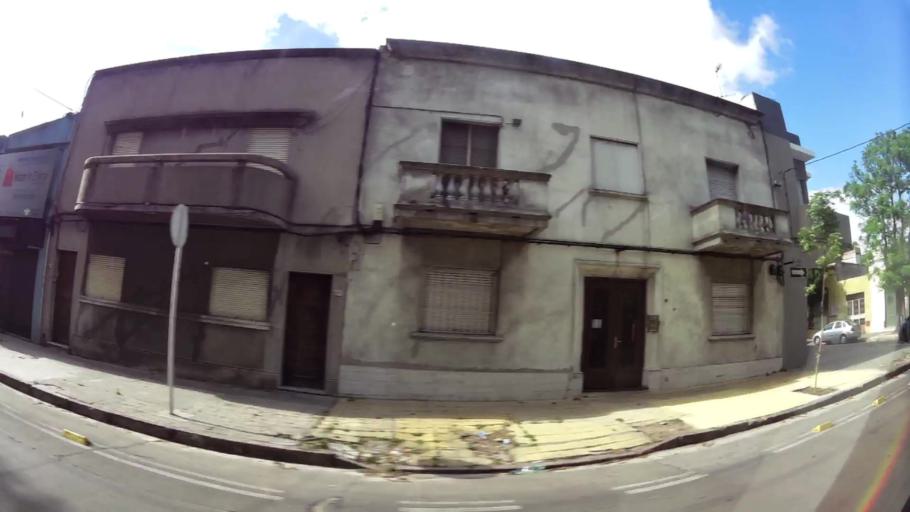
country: UY
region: Montevideo
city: Montevideo
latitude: -34.8882
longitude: -56.1680
